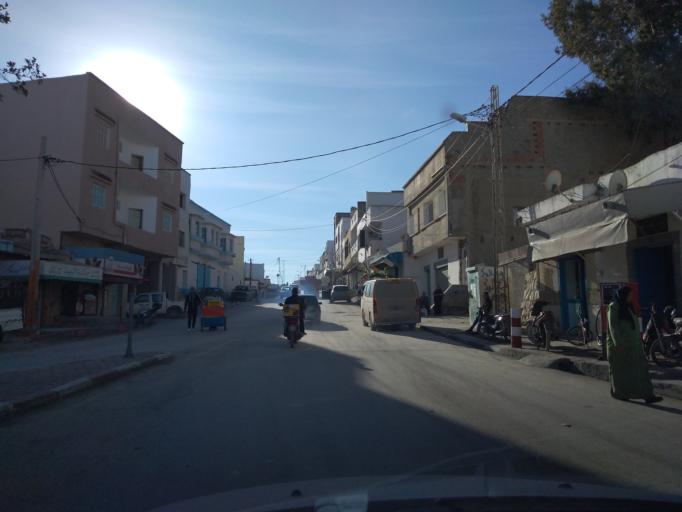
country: TN
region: Ariana
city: Qal'at al Andalus
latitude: 37.0624
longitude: 10.1180
